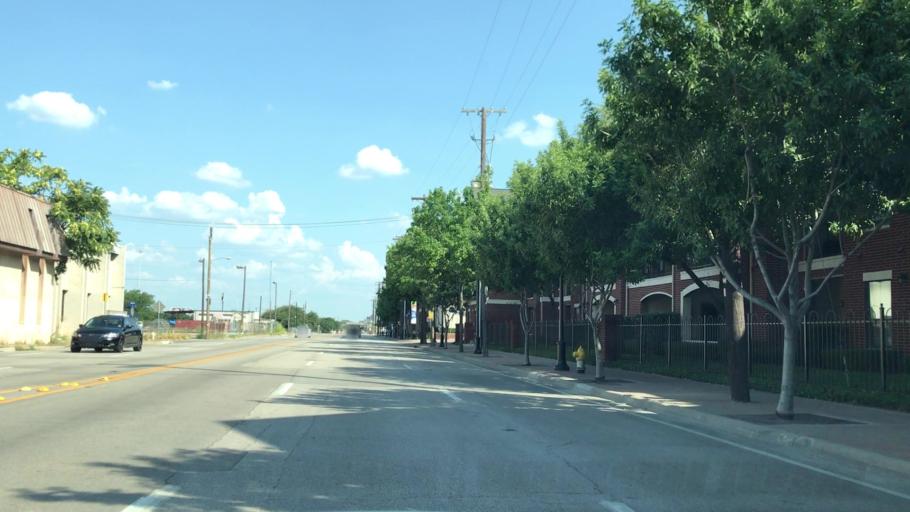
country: US
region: Texas
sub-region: Dallas County
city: Dallas
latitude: 32.7807
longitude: -96.7860
